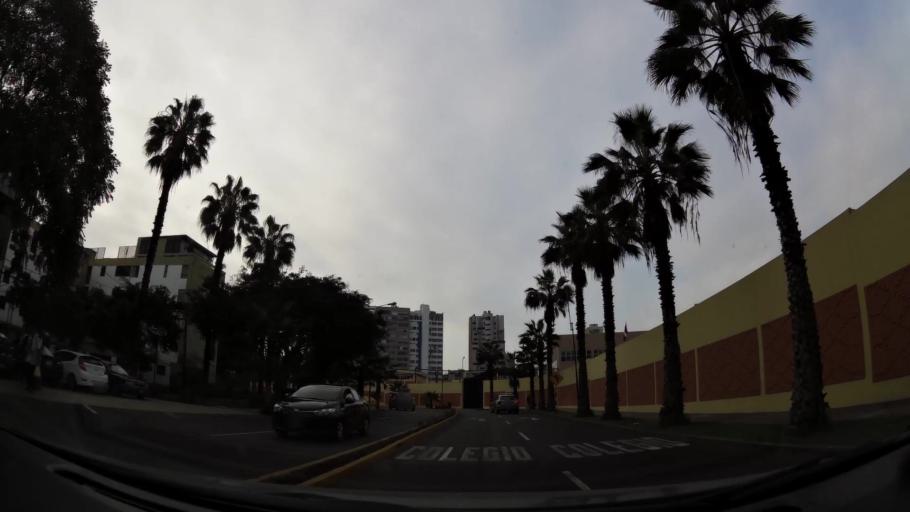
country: PE
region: Lima
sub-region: Lima
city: San Isidro
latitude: -12.1054
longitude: -77.0474
